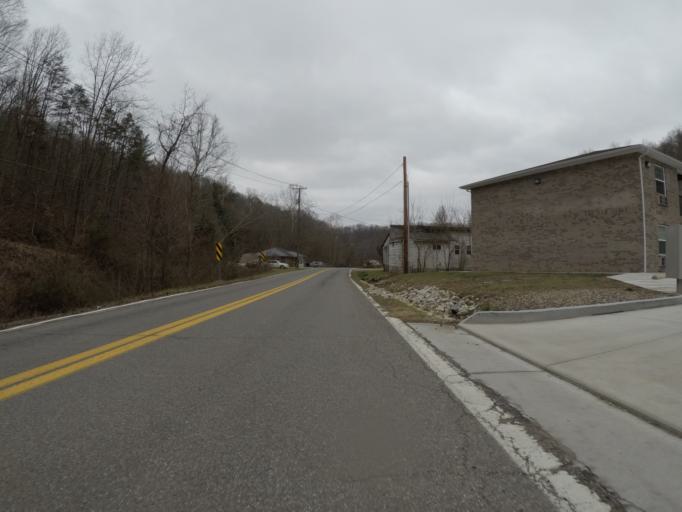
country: US
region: West Virginia
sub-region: Cabell County
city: Barboursville
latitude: 38.4376
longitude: -82.2923
